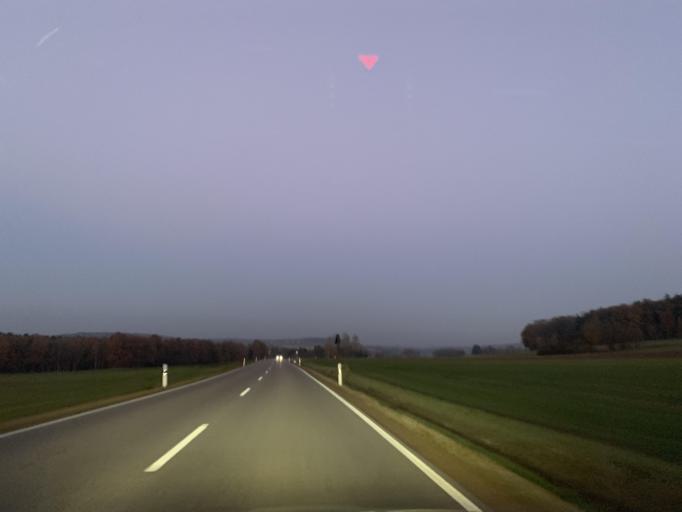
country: DE
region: Bavaria
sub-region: Upper Palatinate
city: Bruck in der Oberpfalz
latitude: 49.2509
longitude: 12.2815
